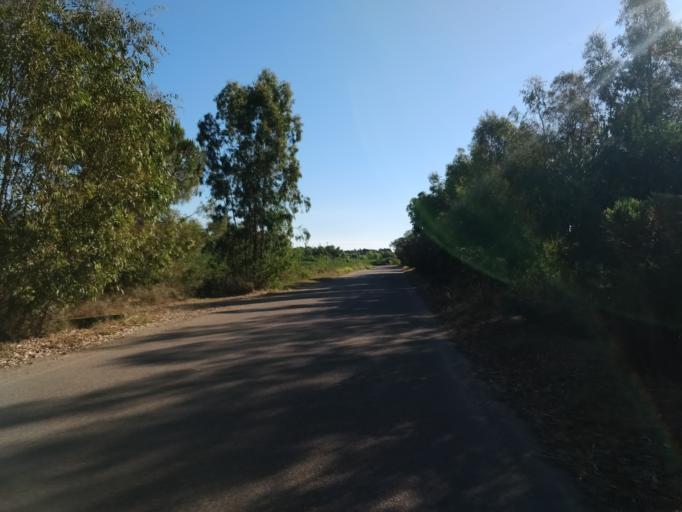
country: IT
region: Sardinia
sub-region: Provincia di Ogliastra
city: Girasole
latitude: 39.9573
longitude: 9.6759
